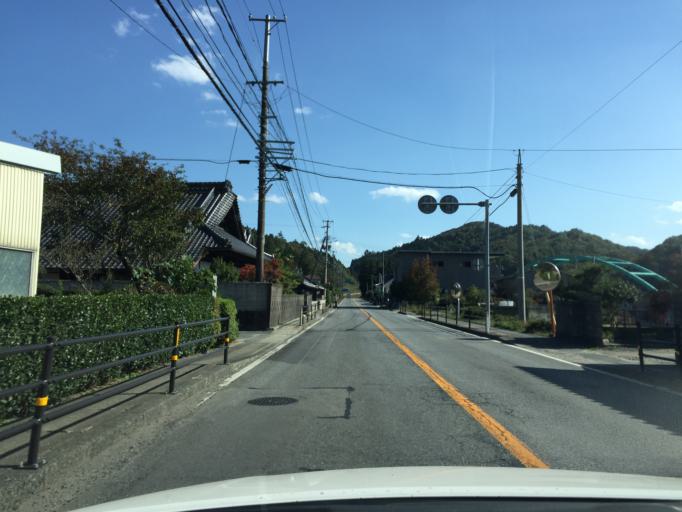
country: JP
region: Fukushima
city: Iwaki
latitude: 37.1001
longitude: 140.7753
